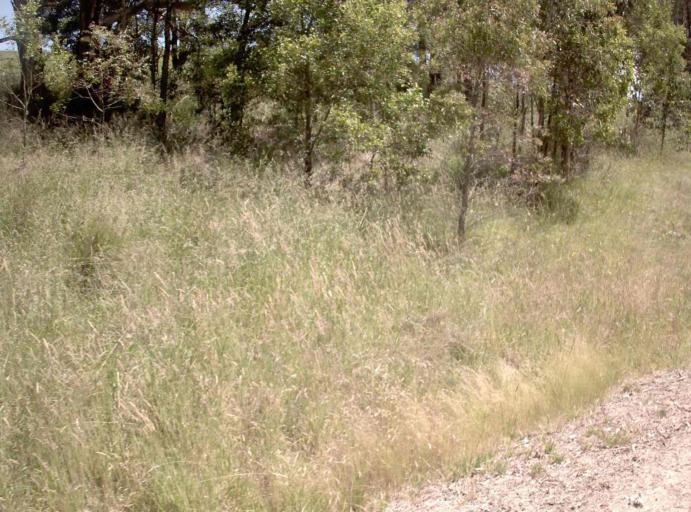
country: AU
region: Victoria
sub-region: East Gippsland
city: Lakes Entrance
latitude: -37.2123
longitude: 148.2687
